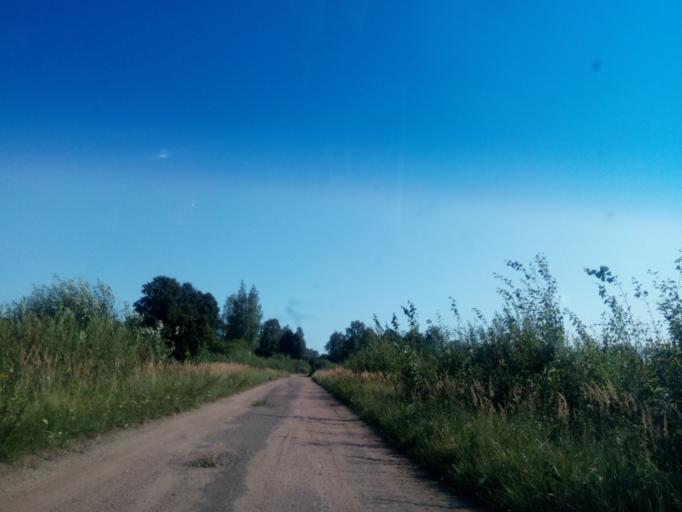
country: BY
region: Vitebsk
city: Dzisna
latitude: 55.6482
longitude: 28.2540
